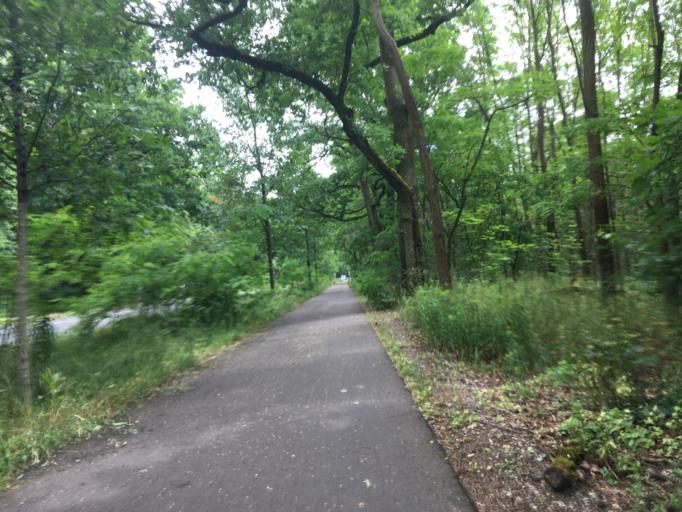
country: DE
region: Brandenburg
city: Erkner
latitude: 52.4304
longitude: 13.7313
